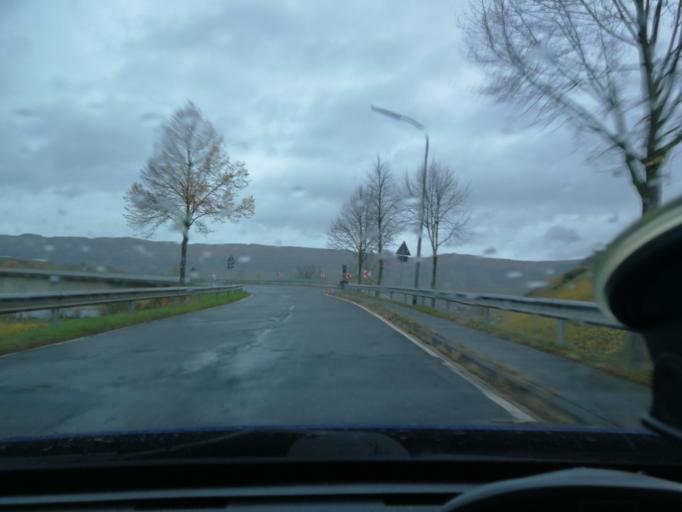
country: DE
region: Rheinland-Pfalz
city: Minheim
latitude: 49.8672
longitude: 6.9299
